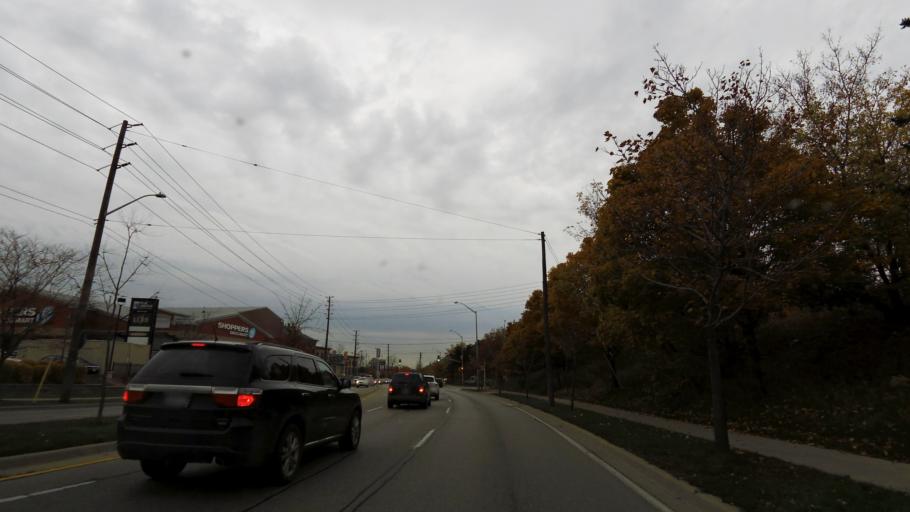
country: CA
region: Ontario
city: Oakville
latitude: 43.4570
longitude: -79.6776
